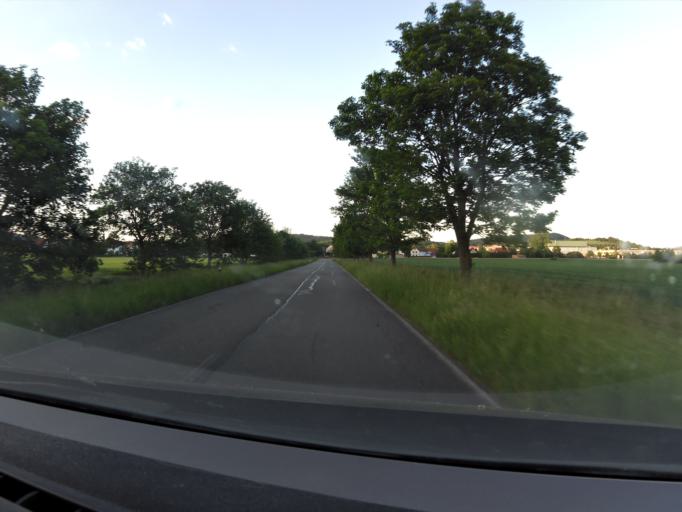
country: DE
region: Thuringia
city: Vacha
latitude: 50.8363
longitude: 10.0348
